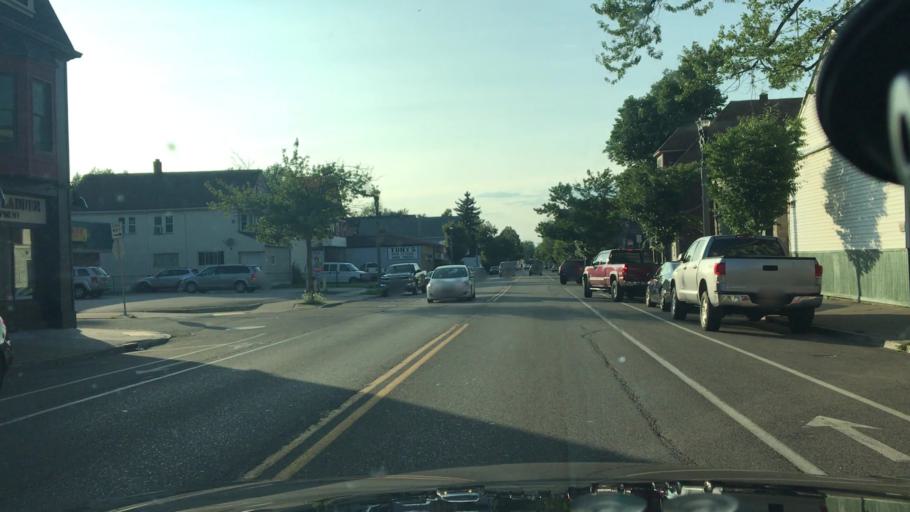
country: US
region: New York
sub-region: Erie County
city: West Seneca
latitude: 42.8546
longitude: -78.8089
